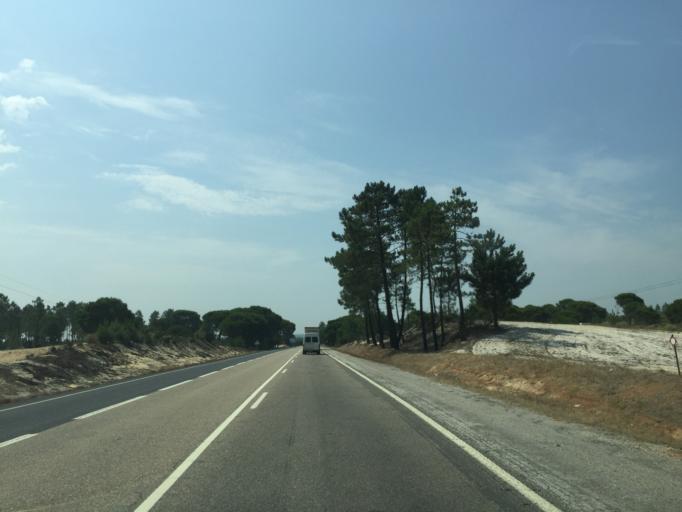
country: PT
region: Setubal
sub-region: Grandola
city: Grandola
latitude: 38.2509
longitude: -8.5479
